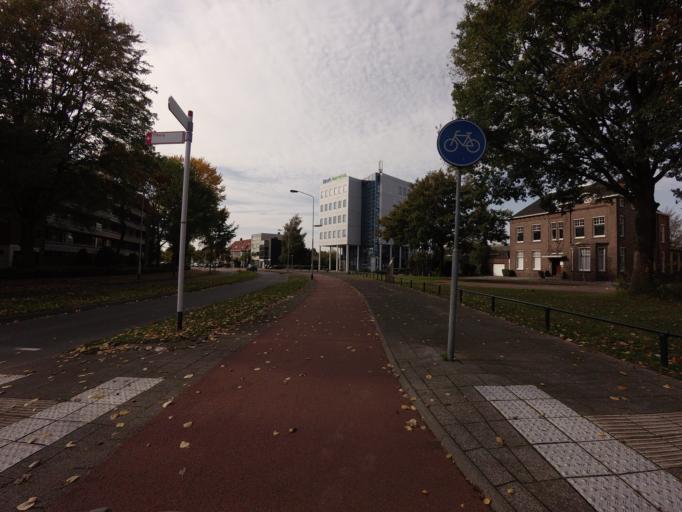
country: NL
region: North Brabant
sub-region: Gemeente Breda
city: Hoge Vucht
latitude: 51.5953
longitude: 4.8085
